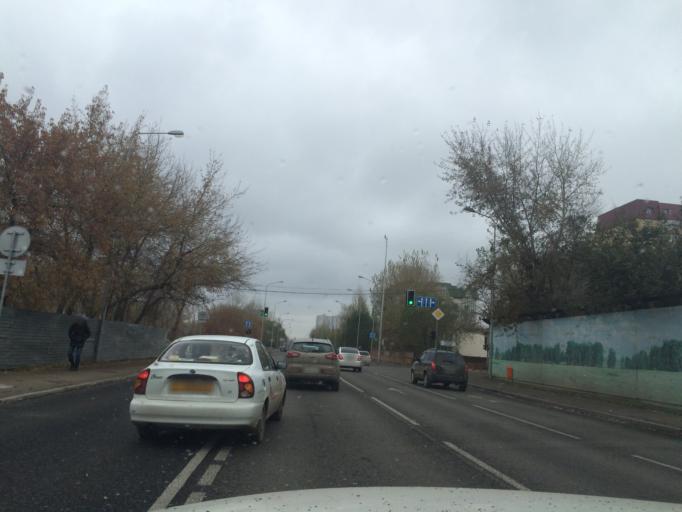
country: KZ
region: Astana Qalasy
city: Astana
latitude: 51.1704
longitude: 71.4498
